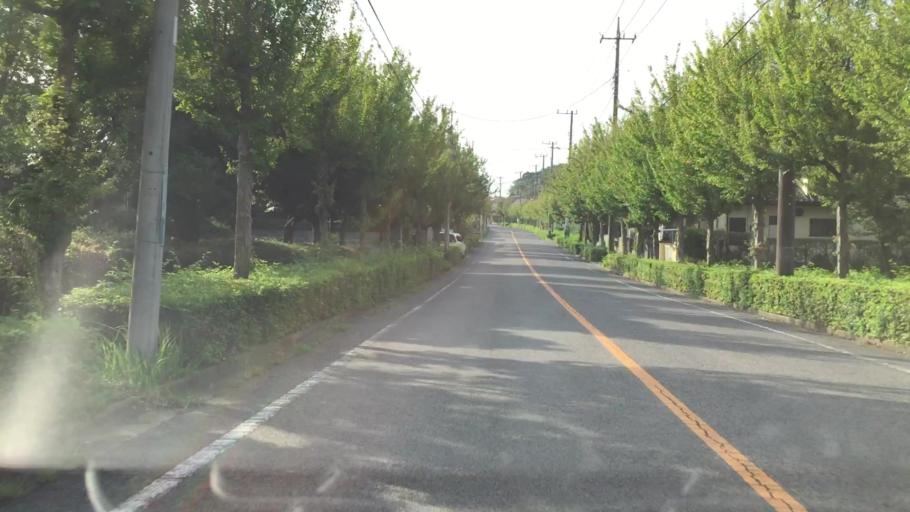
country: JP
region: Ibaraki
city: Toride
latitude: 35.8595
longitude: 140.1163
